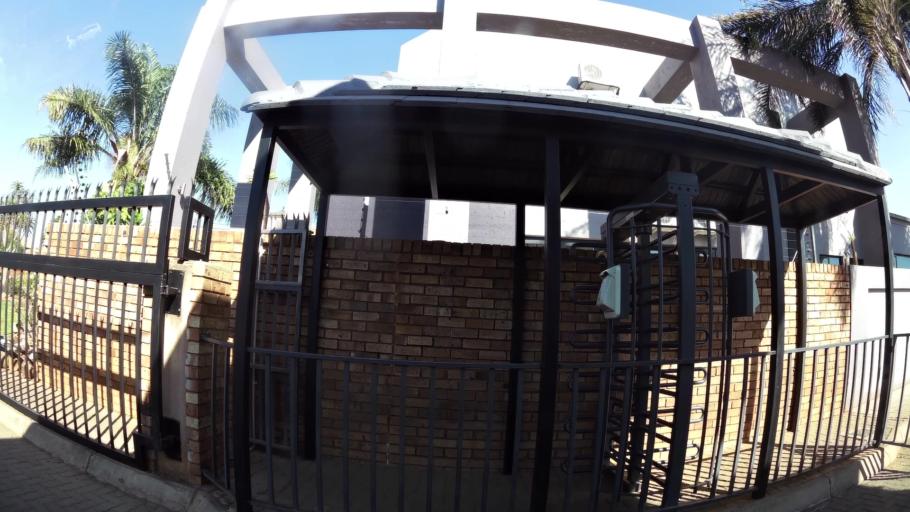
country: ZA
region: Gauteng
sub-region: City of Tshwane Metropolitan Municipality
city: Pretoria
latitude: -25.6642
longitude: 28.2553
